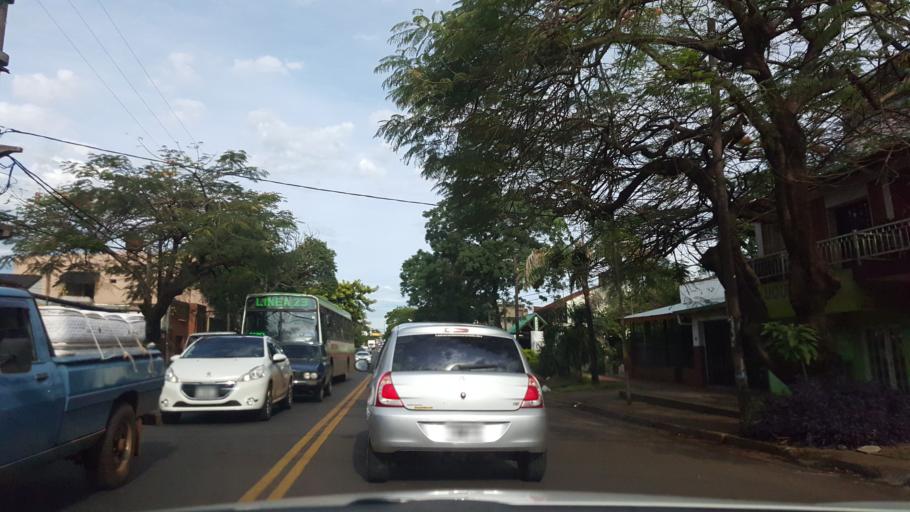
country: AR
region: Misiones
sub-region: Departamento de Capital
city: Posadas
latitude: -27.3731
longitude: -55.9097
